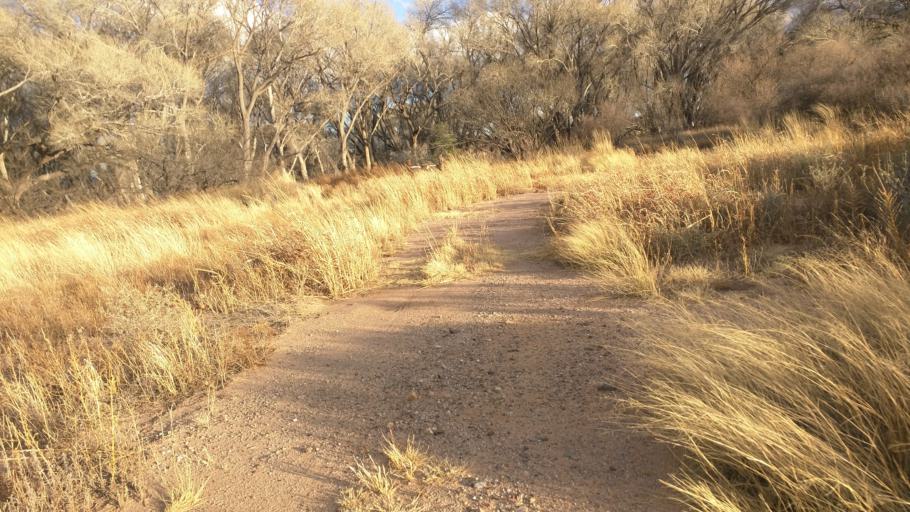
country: US
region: Arizona
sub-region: Cochise County
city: Sierra Vista Southeast
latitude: 31.3681
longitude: -110.1199
